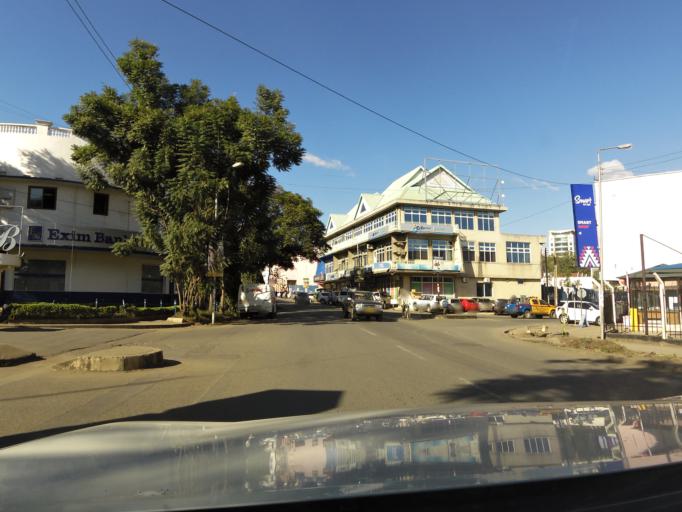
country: TZ
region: Arusha
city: Arusha
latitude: -3.3732
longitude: 36.6926
